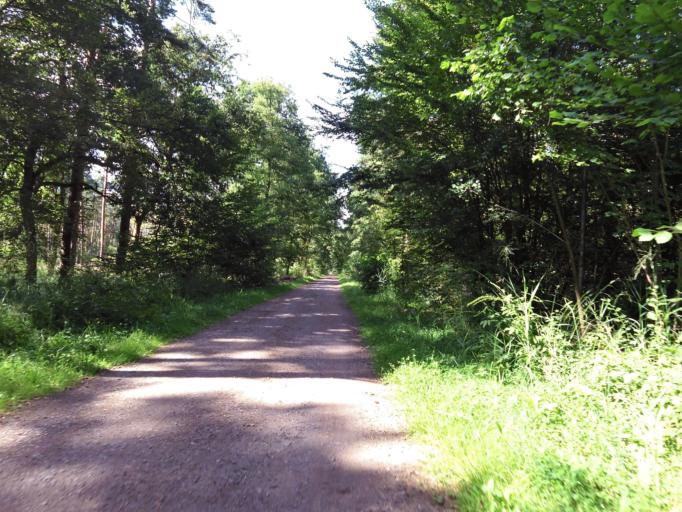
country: DE
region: Rheinland-Pfalz
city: Hanhofen
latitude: 49.3385
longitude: 8.3323
